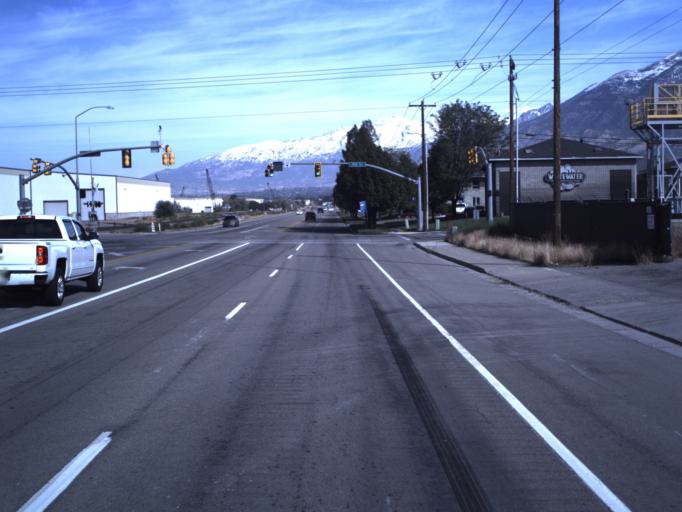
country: US
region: Utah
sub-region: Utah County
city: Lindon
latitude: 40.3329
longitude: -111.7385
